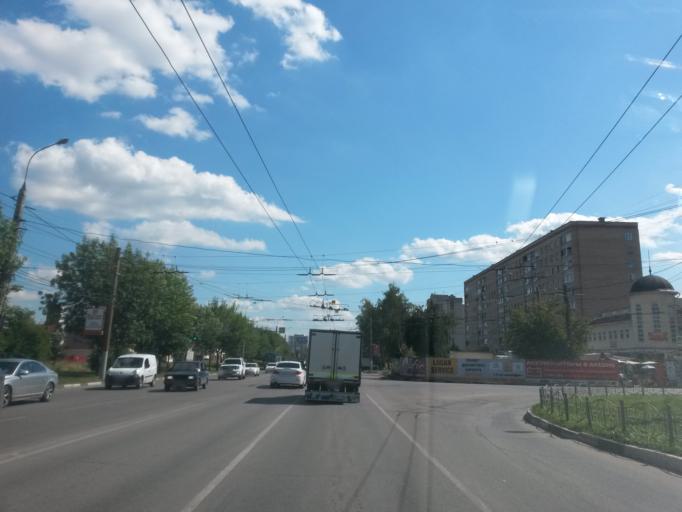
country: RU
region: Ivanovo
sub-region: Gorod Ivanovo
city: Ivanovo
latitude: 56.9704
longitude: 41.0143
